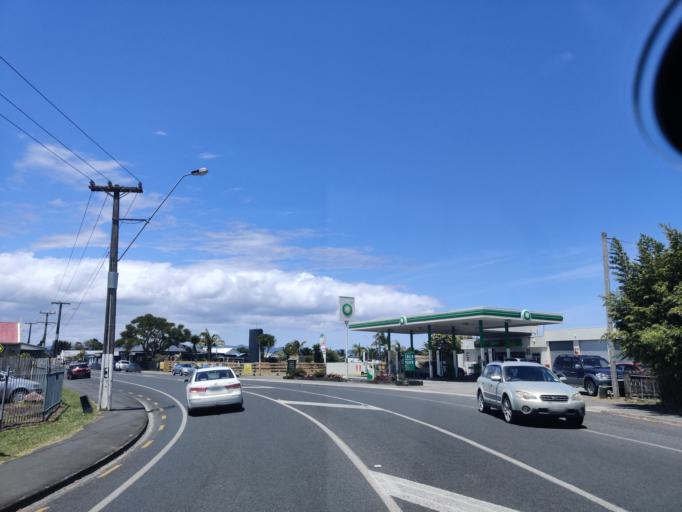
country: NZ
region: Northland
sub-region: Far North District
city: Kaitaia
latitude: -35.0473
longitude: 173.2562
